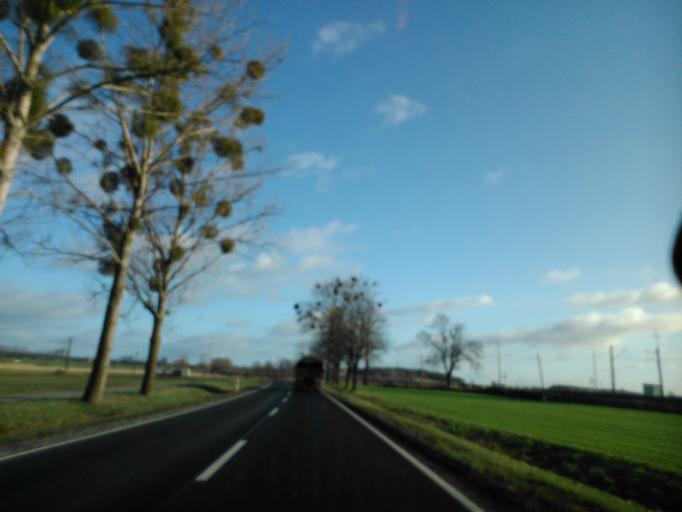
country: PL
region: Kujawsko-Pomorskie
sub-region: Powiat inowroclawski
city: Gniewkowo
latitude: 52.9028
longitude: 18.4553
